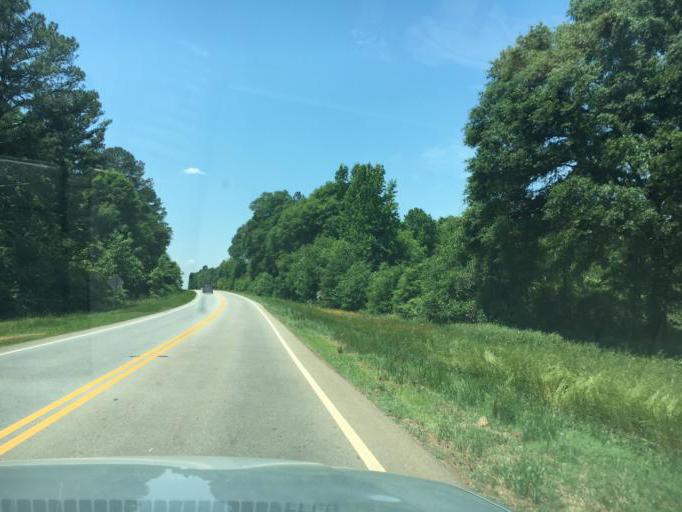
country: US
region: Georgia
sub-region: Hart County
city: Royston
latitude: 34.2891
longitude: -83.0633
